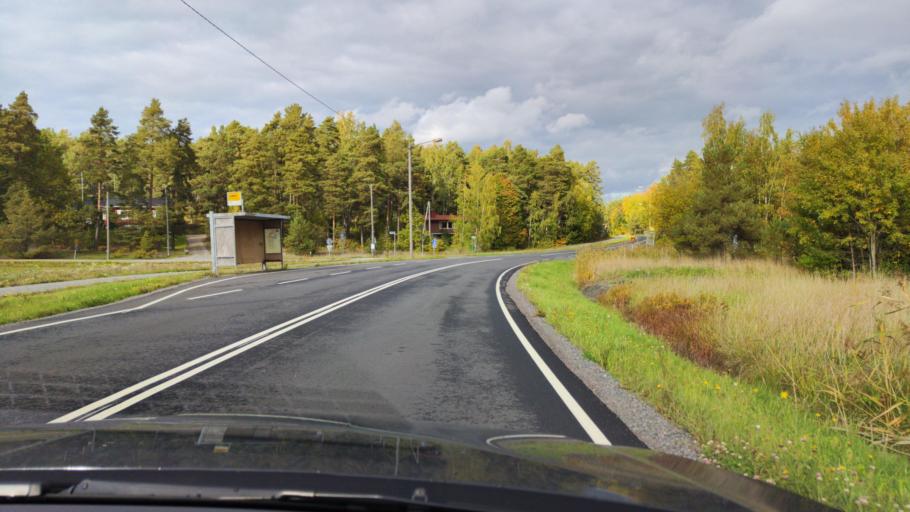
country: FI
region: Varsinais-Suomi
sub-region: Turku
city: Raisio
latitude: 60.3681
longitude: 22.1750
